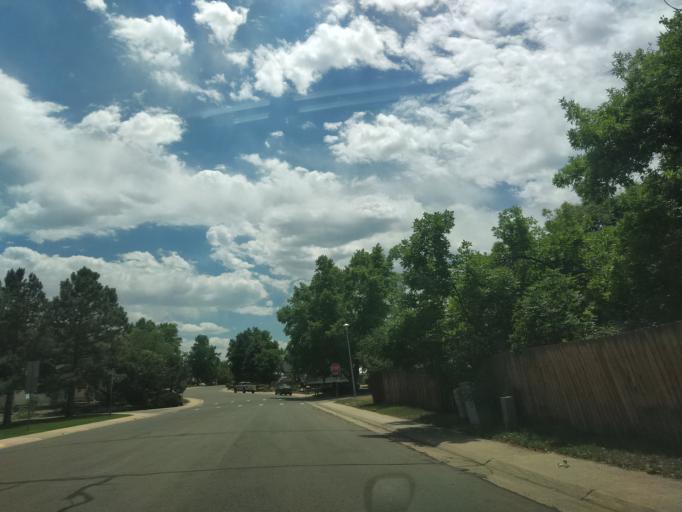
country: US
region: Colorado
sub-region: Jefferson County
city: Lakewood
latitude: 39.6794
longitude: -105.0955
